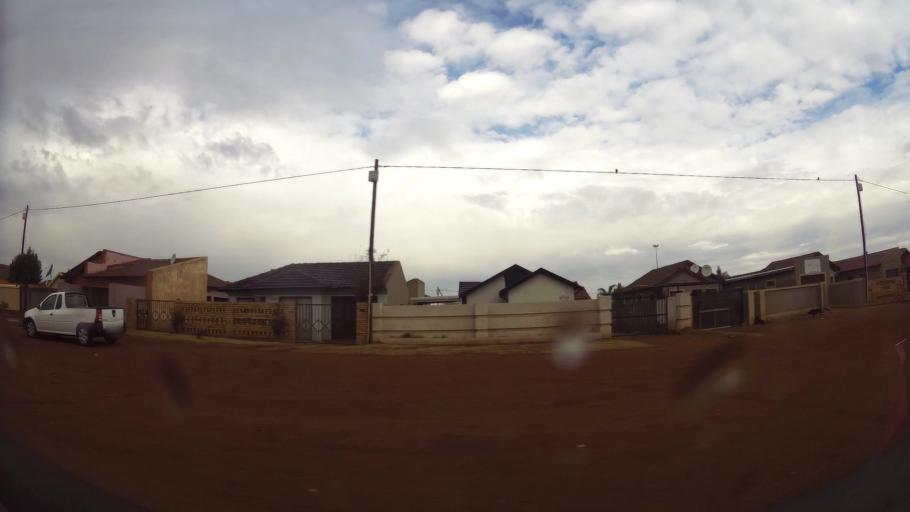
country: ZA
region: Gauteng
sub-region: Ekurhuleni Metropolitan Municipality
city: Germiston
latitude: -26.3307
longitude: 28.2044
